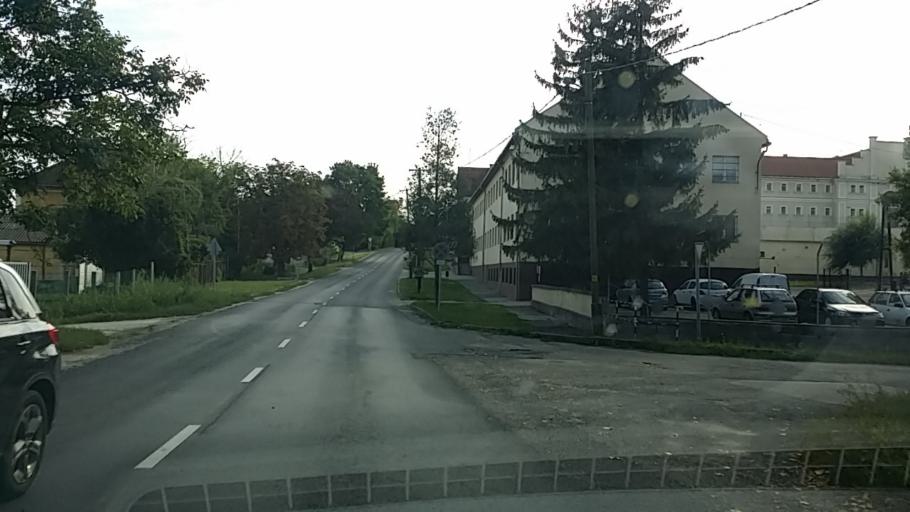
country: HU
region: Gyor-Moson-Sopron
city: Fertorakos
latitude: 47.7256
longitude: 16.6231
